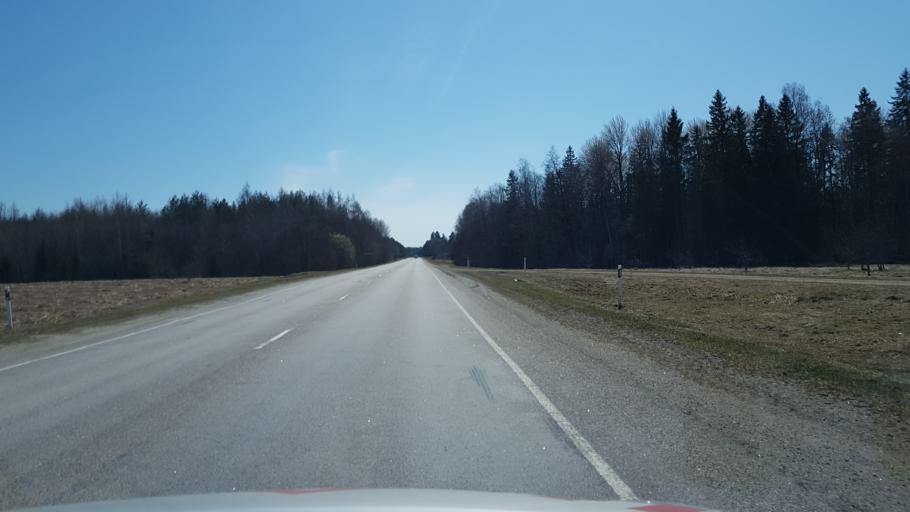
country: EE
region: Ida-Virumaa
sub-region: Johvi vald
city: Johvi
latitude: 59.1726
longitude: 27.3506
